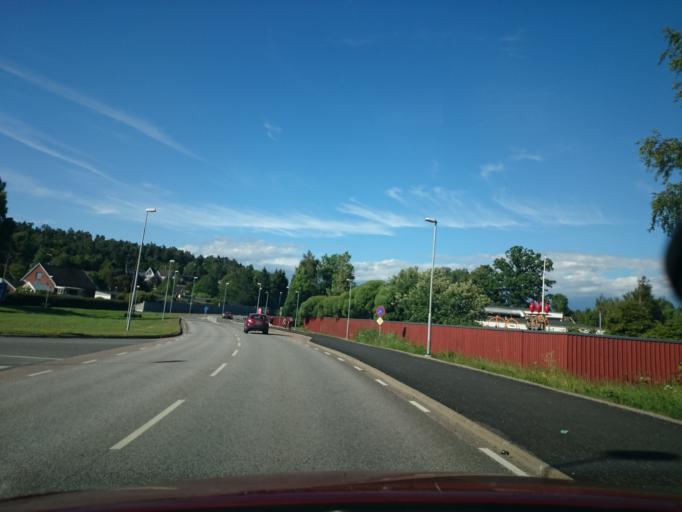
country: SE
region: Vaestra Goetaland
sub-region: Lerums Kommun
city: Lerum
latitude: 57.7757
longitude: 12.2767
